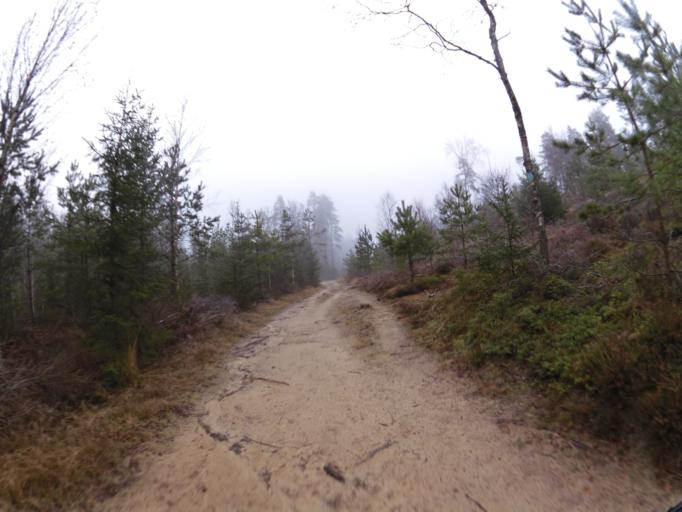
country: NO
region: Ostfold
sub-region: Fredrikstad
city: Fredrikstad
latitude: 59.2633
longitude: 10.9840
